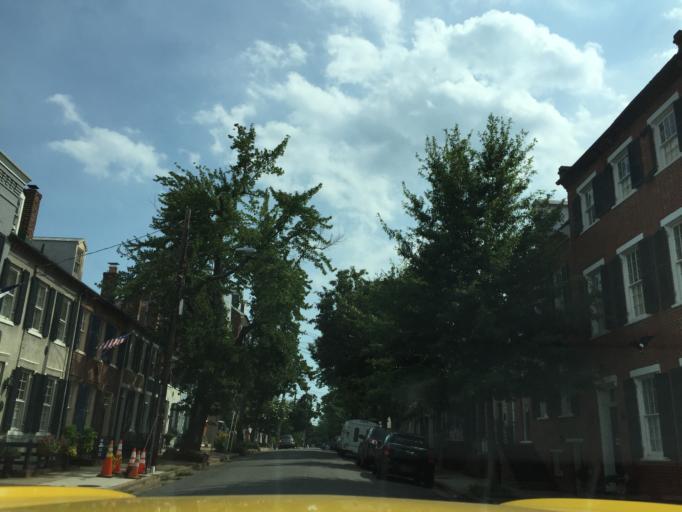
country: US
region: Virginia
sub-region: City of Alexandria
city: Alexandria
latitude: 38.8010
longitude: -77.0422
